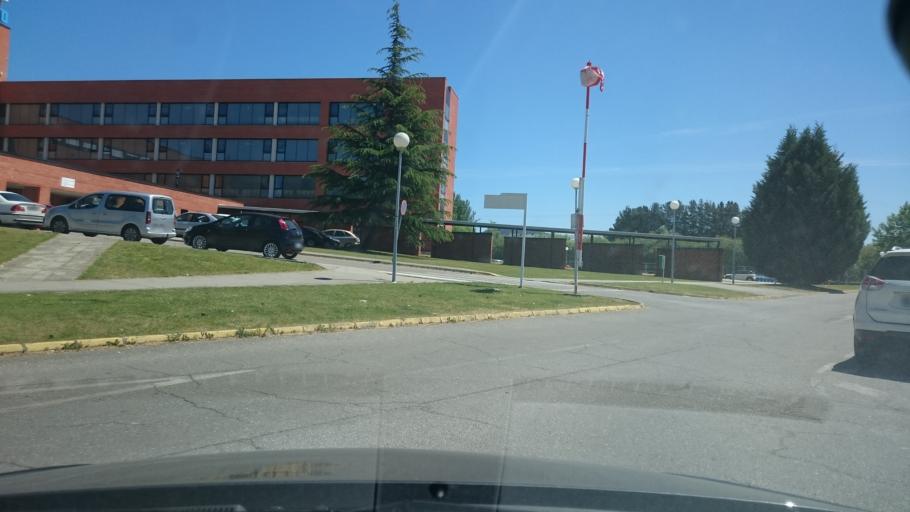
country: ES
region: Castille and Leon
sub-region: Provincia de Leon
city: Camponaraya
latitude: 42.5710
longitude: -6.6441
